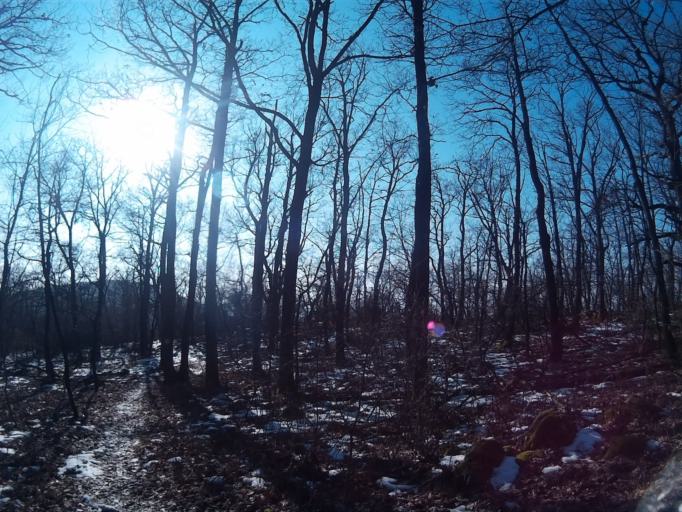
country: HU
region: Nograd
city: Paszto
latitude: 47.9550
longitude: 19.6432
